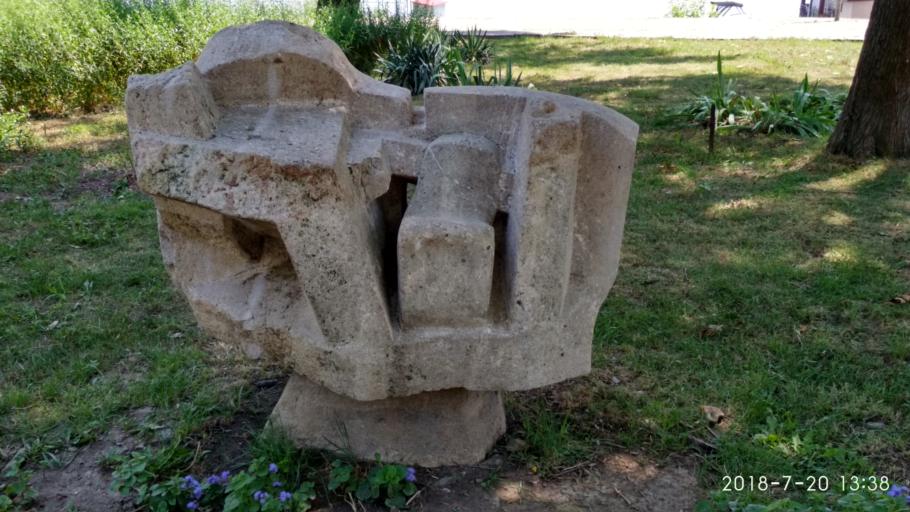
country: RO
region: Braila
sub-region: Municipiul Braila
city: Braila
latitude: 45.2664
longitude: 27.9756
